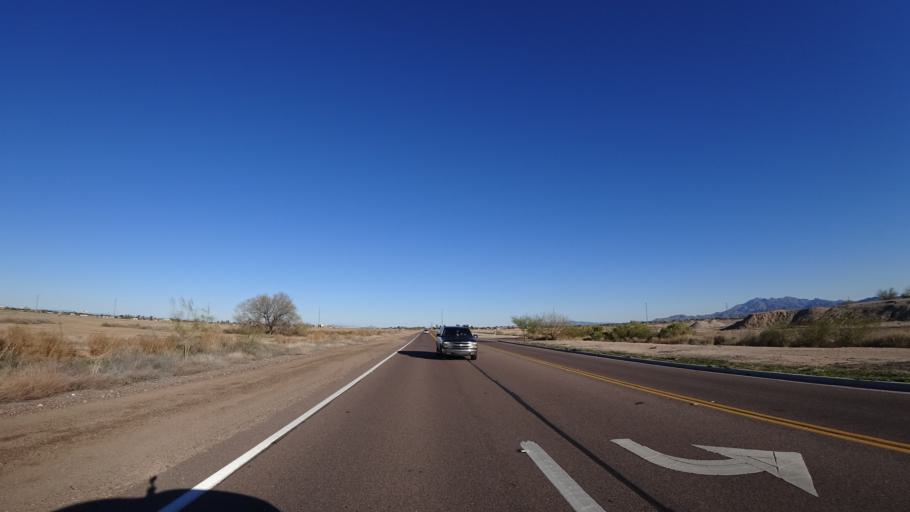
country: US
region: Arizona
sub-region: Maricopa County
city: Citrus Park
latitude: 33.4502
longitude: -112.4693
